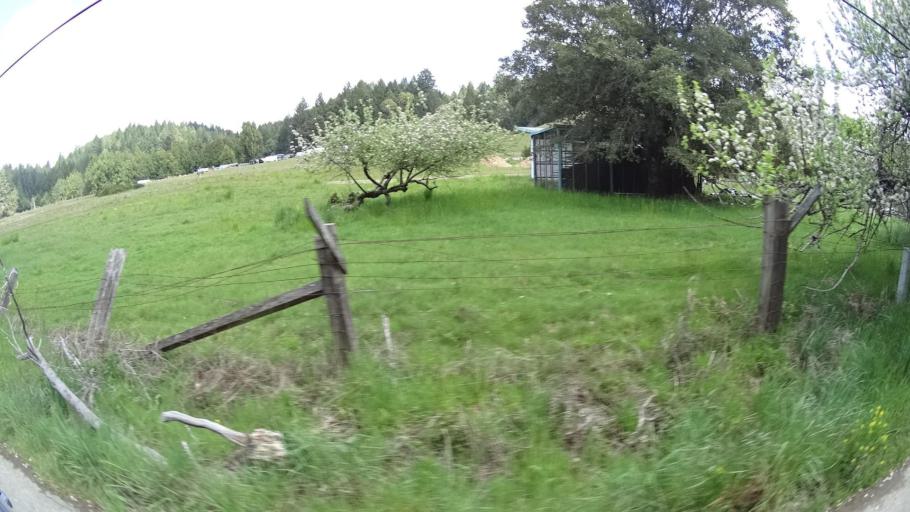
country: US
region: California
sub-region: Humboldt County
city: Redway
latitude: 40.0409
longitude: -123.9585
